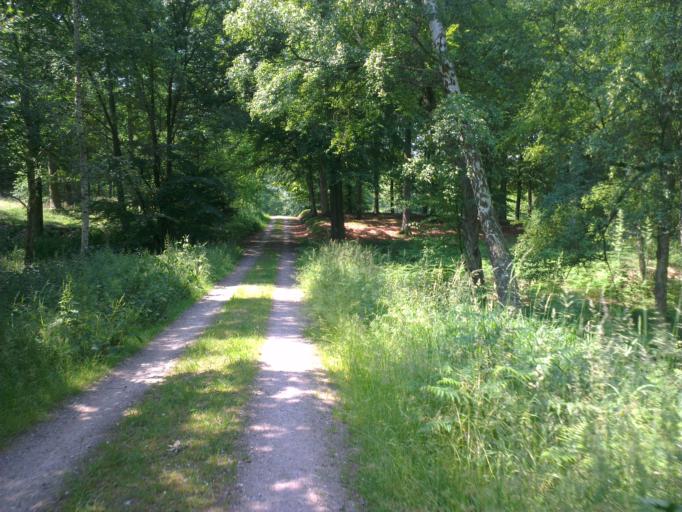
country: DK
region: Capital Region
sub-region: Allerod Kommune
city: Lillerod
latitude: 55.9143
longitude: 12.3619
